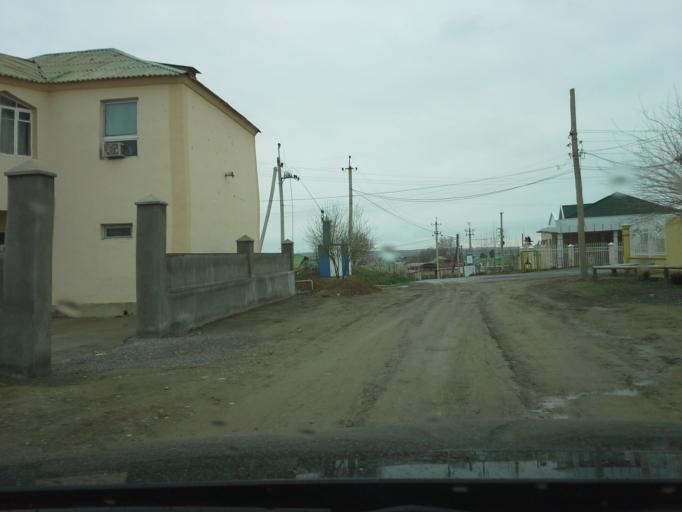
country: TM
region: Ahal
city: Abadan
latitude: 37.9603
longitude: 58.2280
